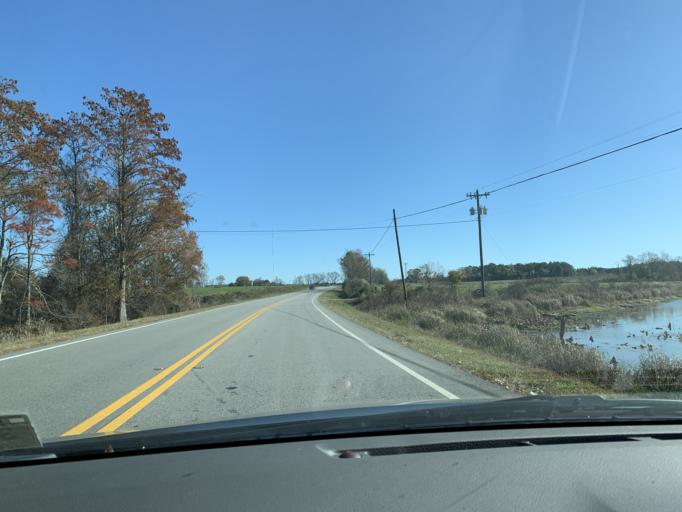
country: US
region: Georgia
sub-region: Ben Hill County
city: Fitzgerald
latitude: 31.7142
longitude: -83.1828
